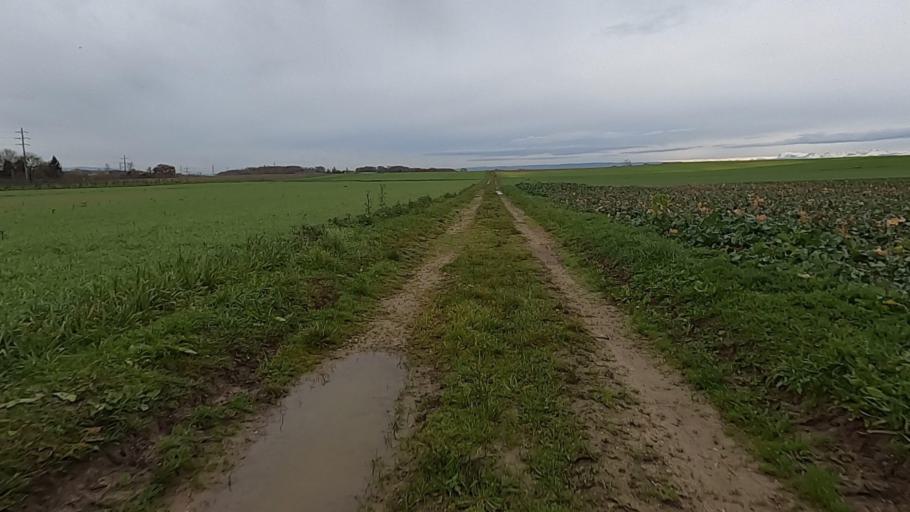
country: CH
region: Vaud
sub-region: Morges District
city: Apples
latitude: 46.5230
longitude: 6.4434
